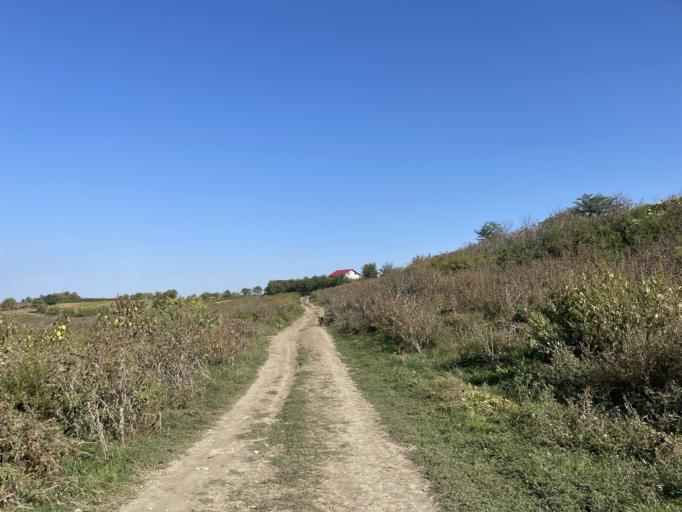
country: RO
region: Iasi
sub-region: Comuna Dumesti
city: Pausesti
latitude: 47.1521
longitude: 27.3153
